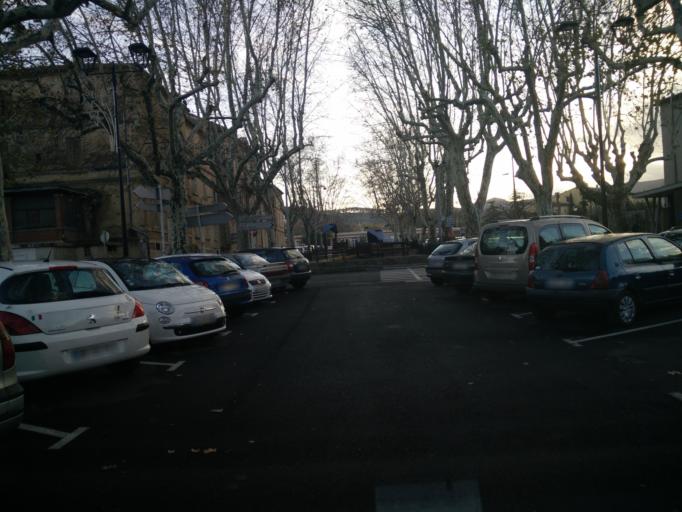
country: FR
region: Provence-Alpes-Cote d'Azur
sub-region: Departement du Var
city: Brignoles
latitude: 43.4053
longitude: 6.0650
